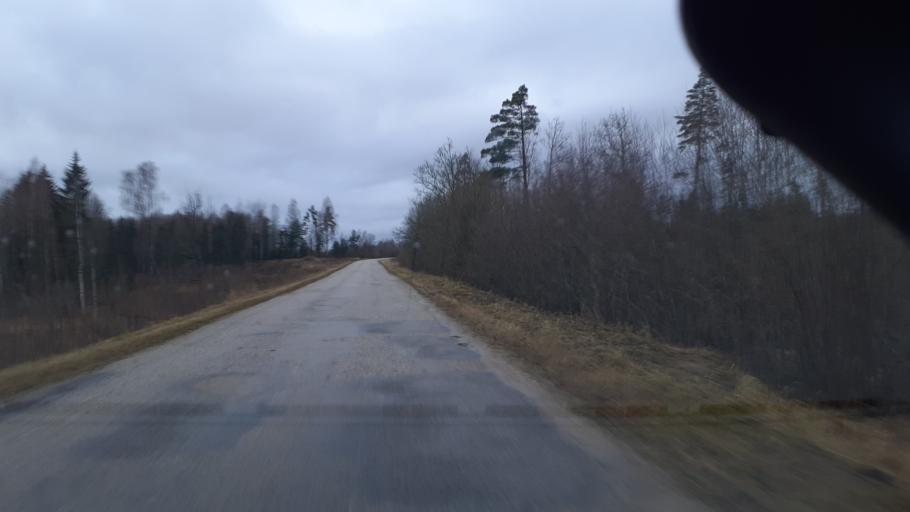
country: LV
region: Kuldigas Rajons
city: Kuldiga
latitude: 56.8729
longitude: 21.8538
